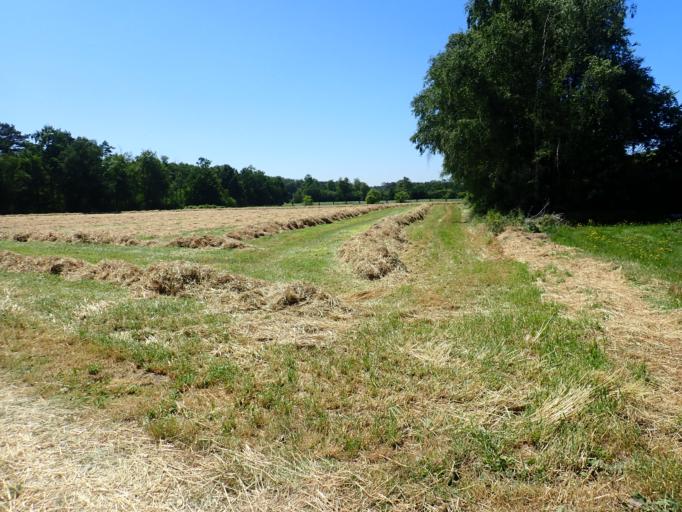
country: BE
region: Flanders
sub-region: Provincie Antwerpen
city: Beerse
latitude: 51.2910
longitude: 4.8229
